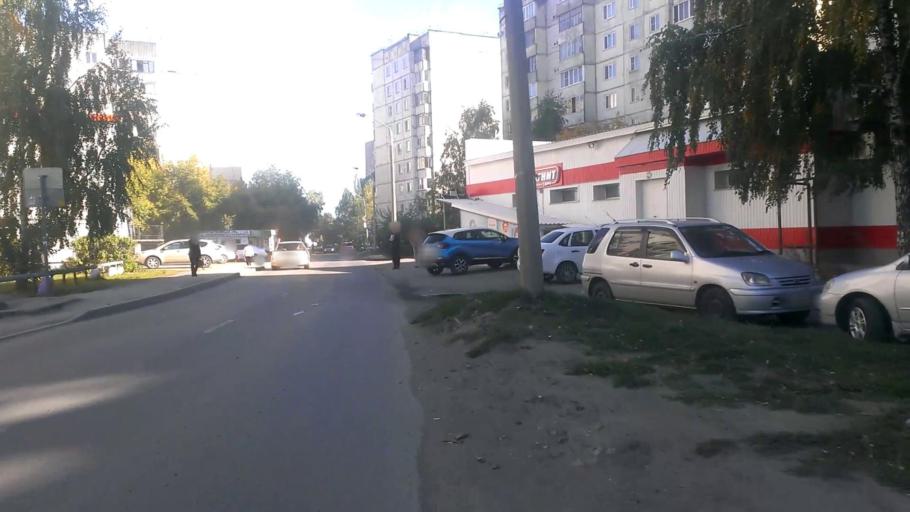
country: RU
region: Altai Krai
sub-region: Gorod Barnaulskiy
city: Barnaul
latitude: 53.3740
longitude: 83.6894
